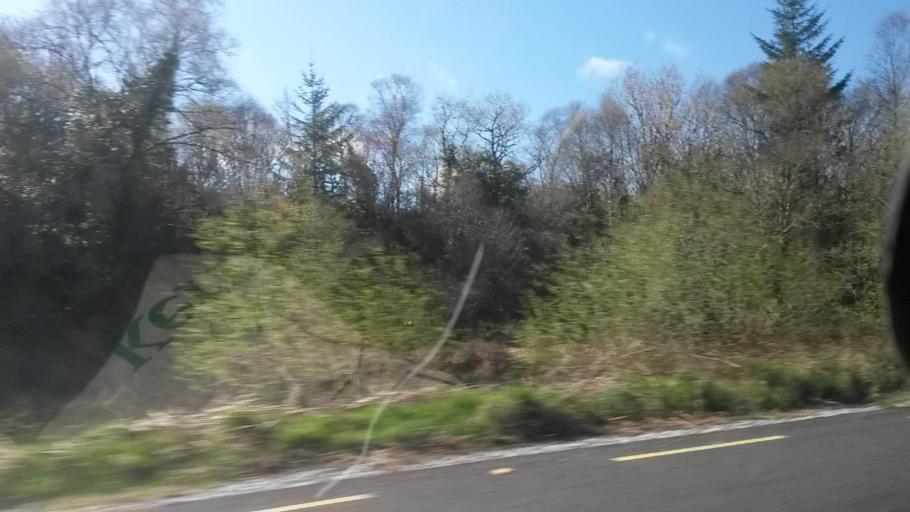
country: IE
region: Munster
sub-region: Ciarrai
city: Cill Airne
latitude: 51.9553
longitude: -9.3877
